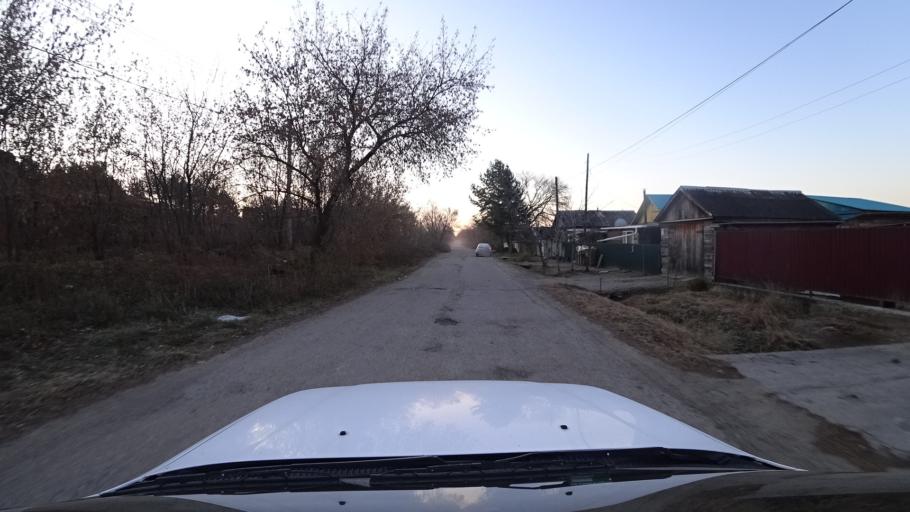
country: RU
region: Primorskiy
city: Dal'nerechensk
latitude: 45.9211
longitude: 133.7361
